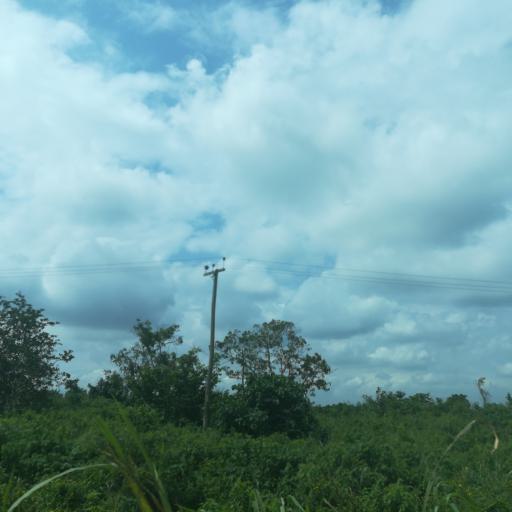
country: NG
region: Lagos
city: Ikorodu
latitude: 6.6530
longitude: 3.6993
